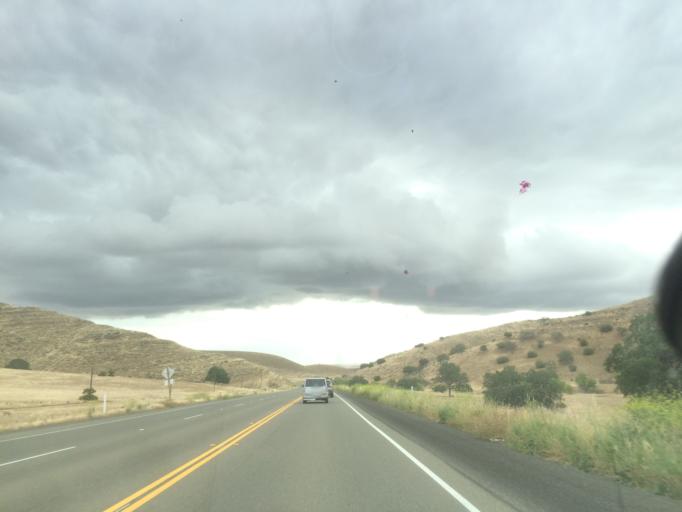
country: US
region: California
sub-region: Kings County
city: Avenal
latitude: 35.7733
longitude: -120.1596
